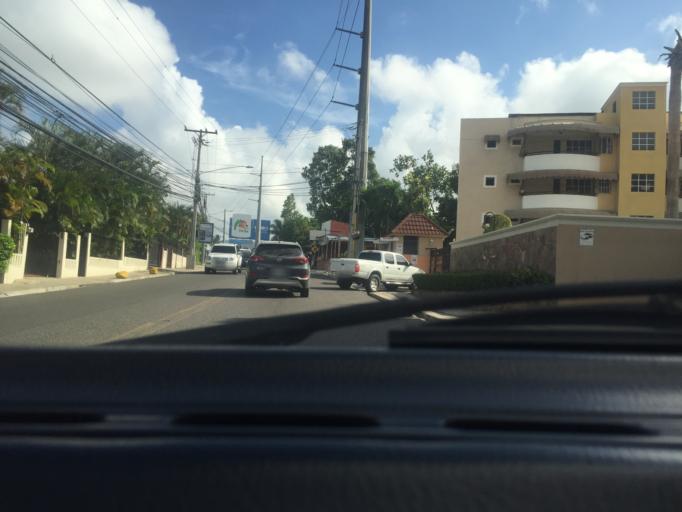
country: DO
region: Santiago
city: Santiago de los Caballeros
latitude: 19.4527
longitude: -70.6655
